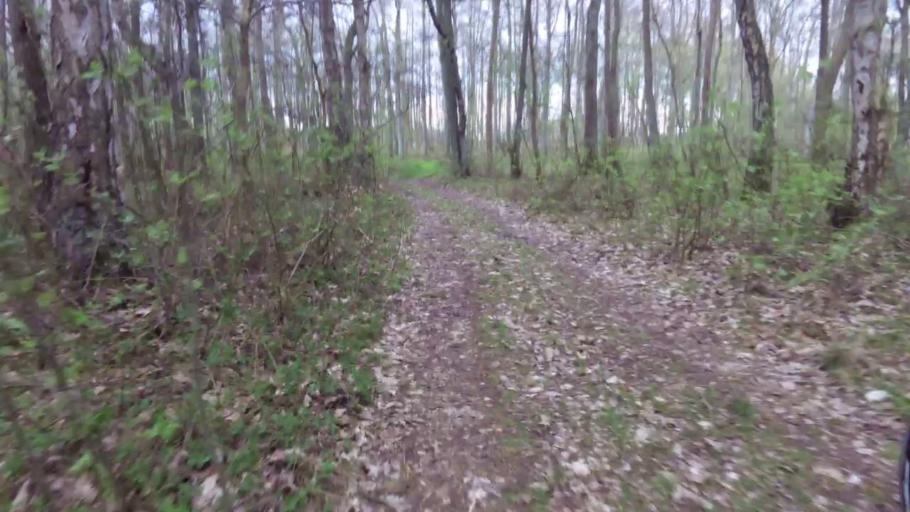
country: PL
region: West Pomeranian Voivodeship
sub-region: Powiat kamienski
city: Dziwnow
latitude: 53.9975
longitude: 14.6509
